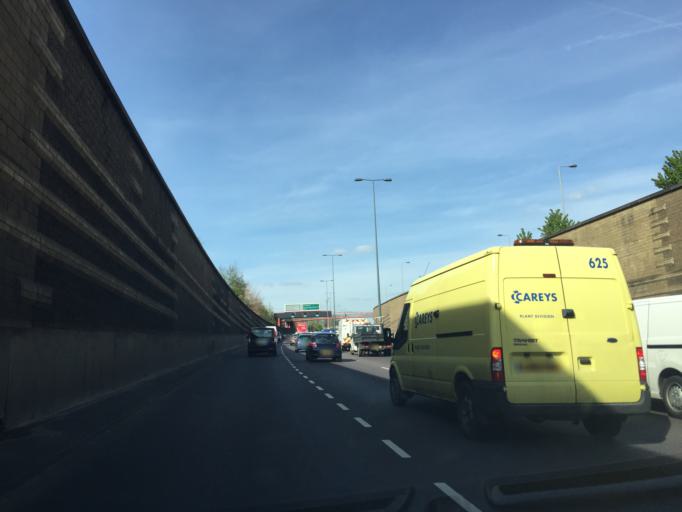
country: GB
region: England
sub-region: Greater London
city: Walthamstow
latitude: 51.5699
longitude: 0.0088
